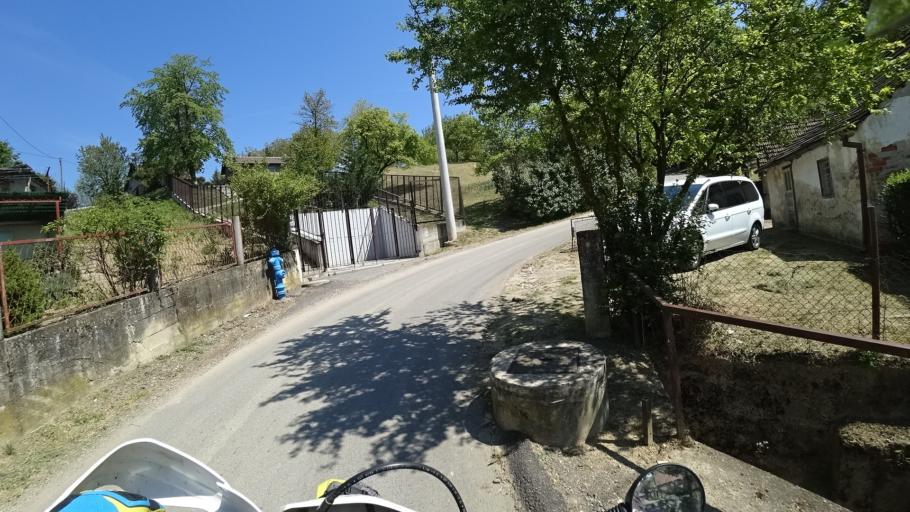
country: HR
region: Zagrebacka
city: Bestovje
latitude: 45.8251
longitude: 15.8311
